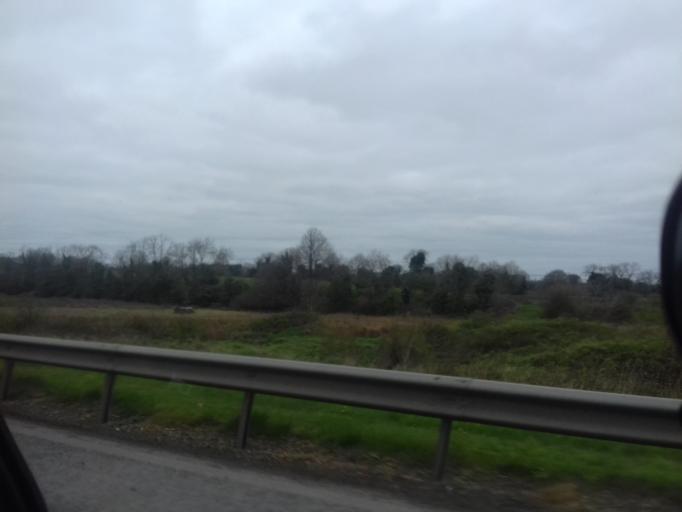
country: IE
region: Leinster
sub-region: An Iarmhi
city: Rathwire
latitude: 53.4792
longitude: -7.1690
